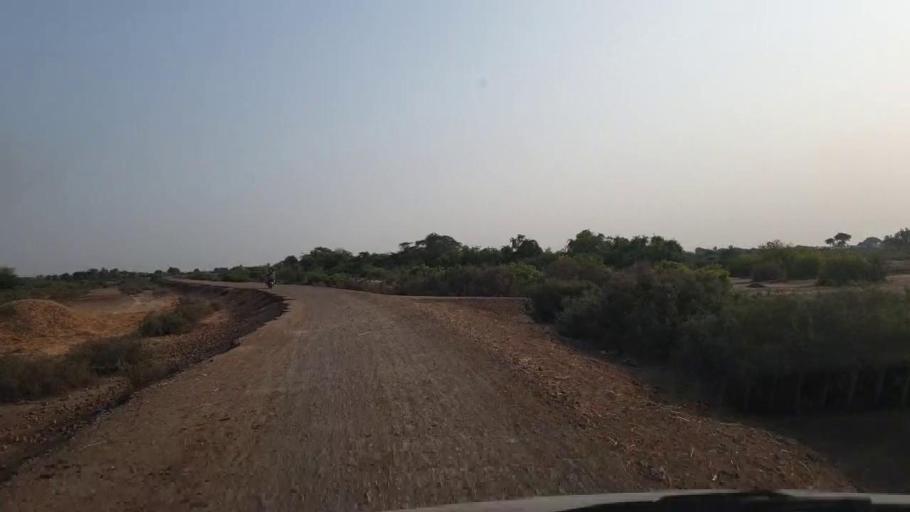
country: PK
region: Sindh
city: Rajo Khanani
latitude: 25.0274
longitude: 68.7787
